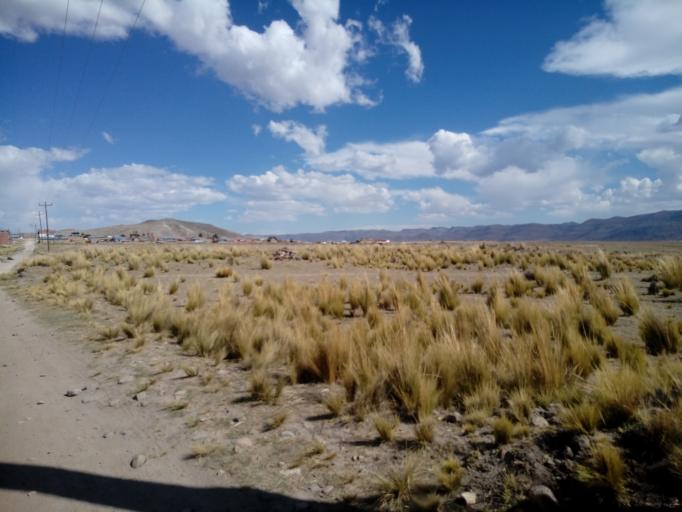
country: PE
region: Puno
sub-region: Provincia de Chucuito
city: Zepita
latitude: -16.4185
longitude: -69.1819
